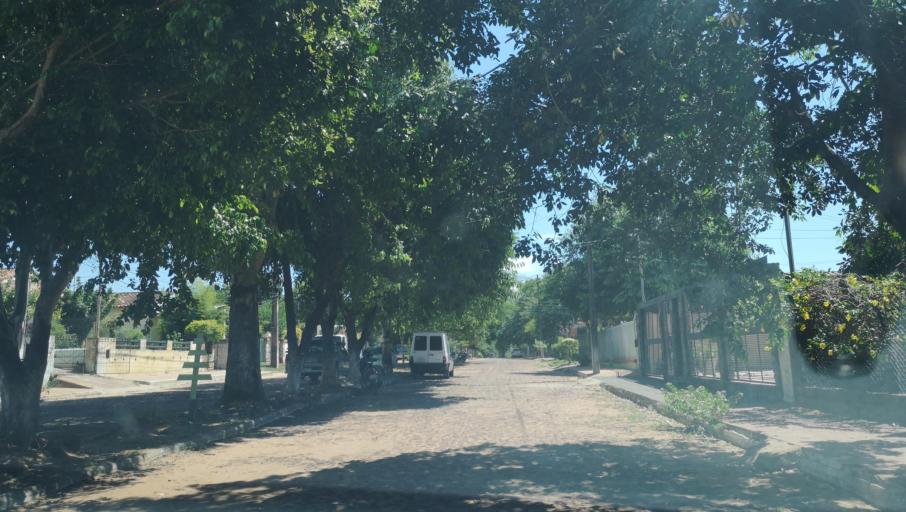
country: PY
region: Misiones
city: Santa Maria
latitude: -26.8806
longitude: -57.0248
